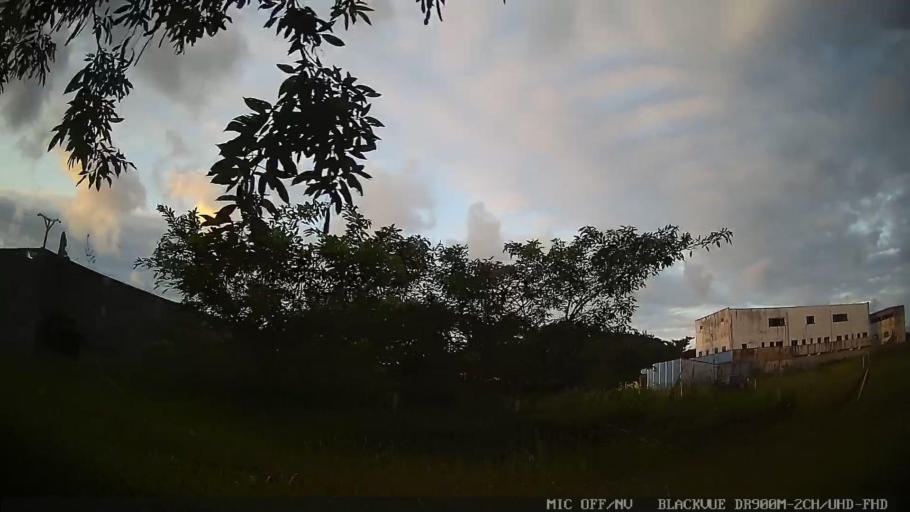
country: BR
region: Sao Paulo
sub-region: Itanhaem
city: Itanhaem
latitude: -24.1876
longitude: -46.8368
